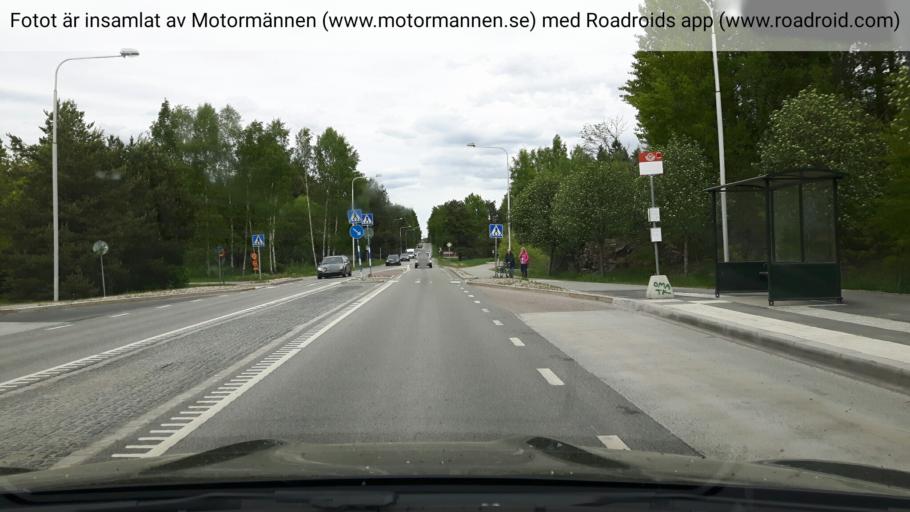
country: SE
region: Stockholm
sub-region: Osterakers Kommun
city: Akersberga
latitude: 59.4859
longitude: 18.3183
